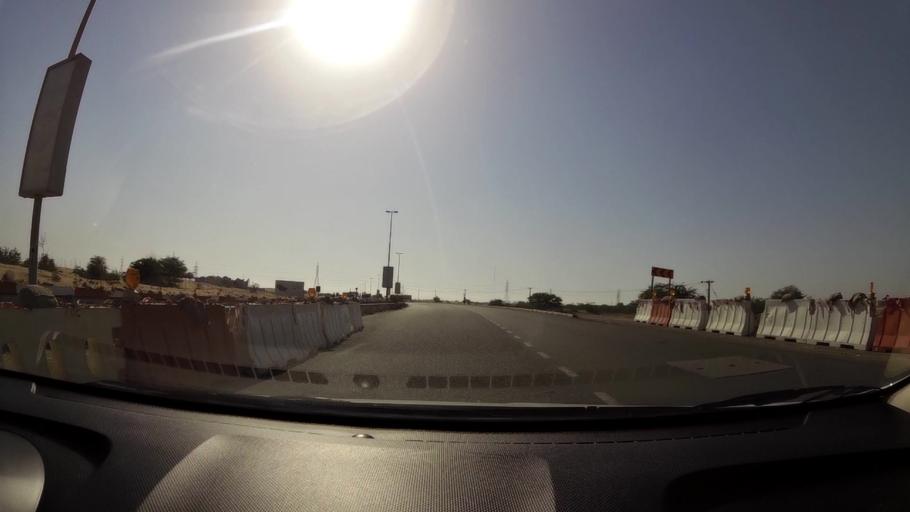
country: AE
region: Umm al Qaywayn
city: Umm al Qaywayn
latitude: 25.4695
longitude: 55.5872
